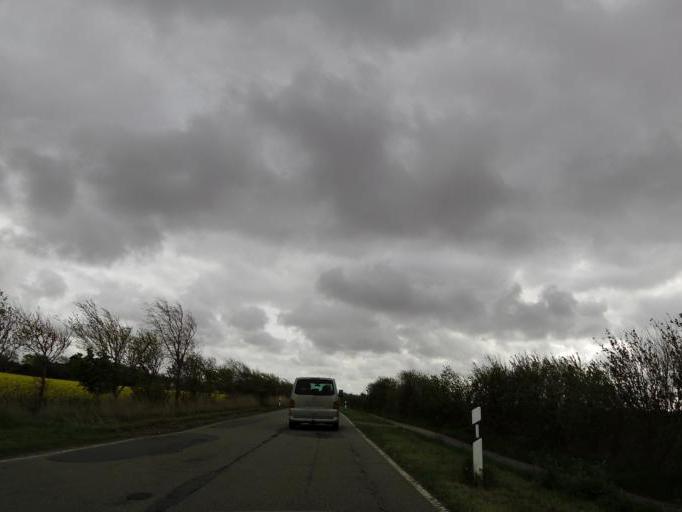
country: DE
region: Schleswig-Holstein
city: Dagebull
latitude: 54.7345
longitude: 8.7150
